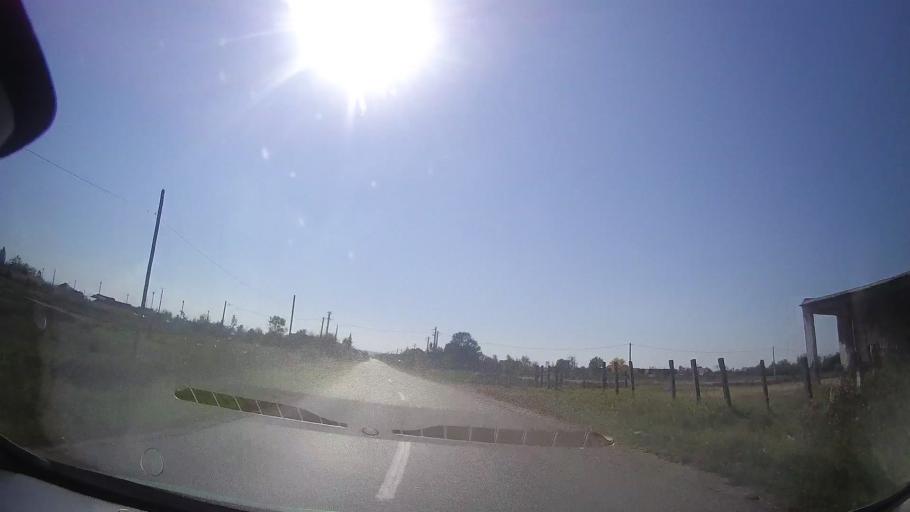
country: RO
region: Timis
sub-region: Comuna Bethausen
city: Bethausen
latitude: 45.8423
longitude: 21.9596
